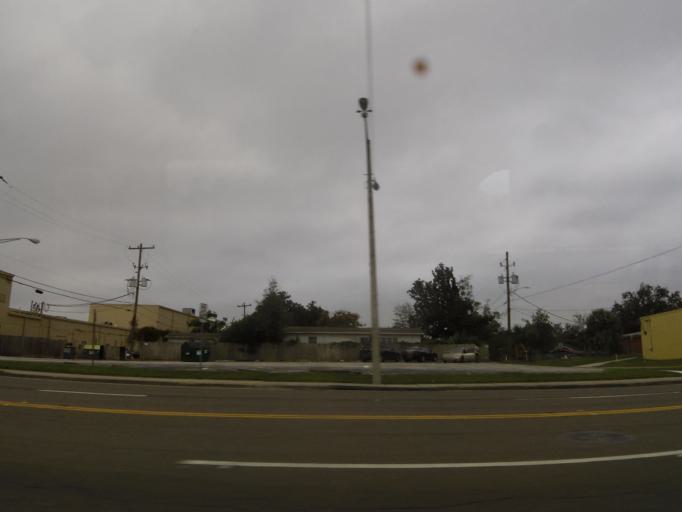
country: US
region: Florida
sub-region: Clay County
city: Bellair-Meadowbrook Terrace
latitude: 30.2705
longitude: -81.7385
